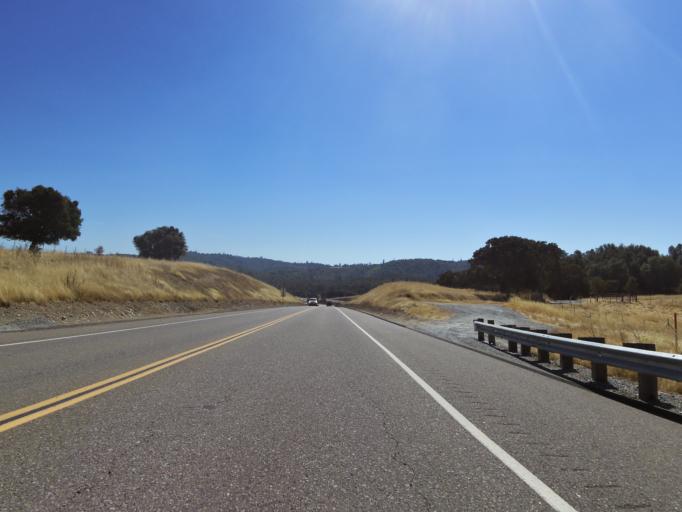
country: US
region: California
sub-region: Calaveras County
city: Angels Camp
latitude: 38.0808
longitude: -120.5351
